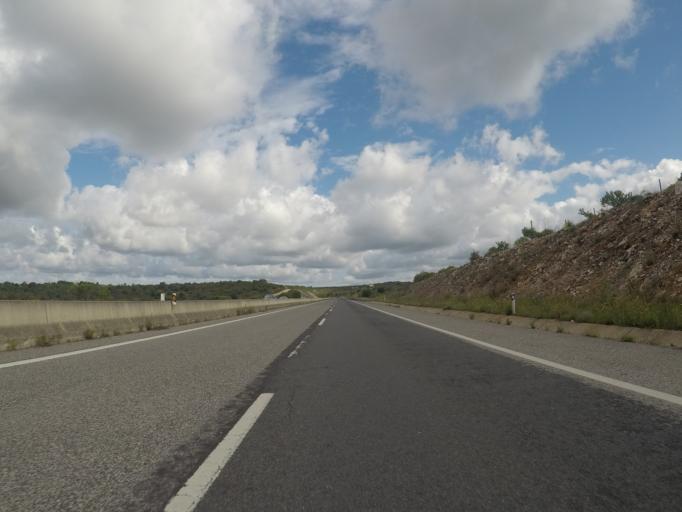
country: PT
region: Faro
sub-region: Lagos
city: Lagos
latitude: 37.1268
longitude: -8.7097
